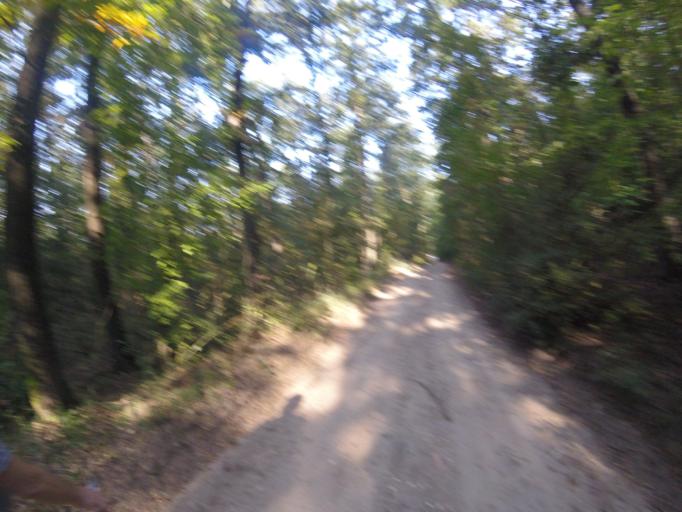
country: HU
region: Komarom-Esztergom
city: Piliscsev
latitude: 47.6910
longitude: 18.8481
